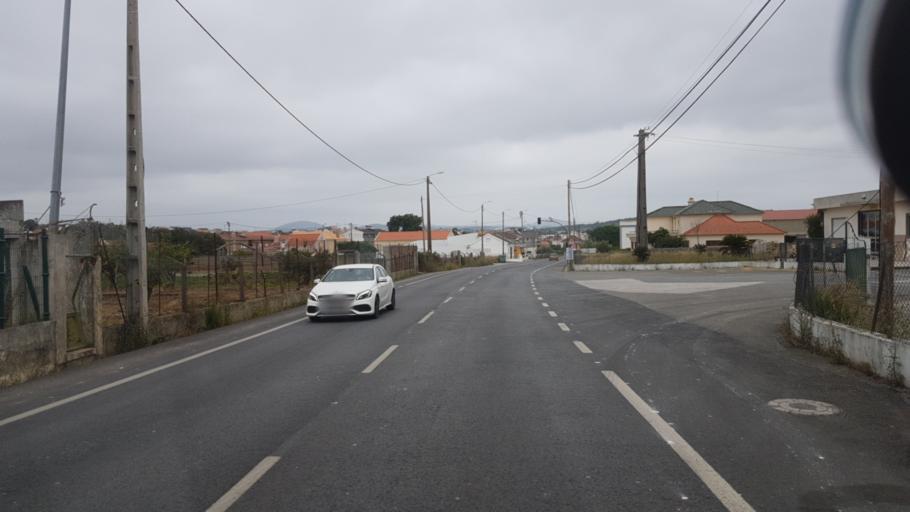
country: PT
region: Lisbon
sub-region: Sintra
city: Pero Pinheiro
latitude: 38.8442
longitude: -9.3378
